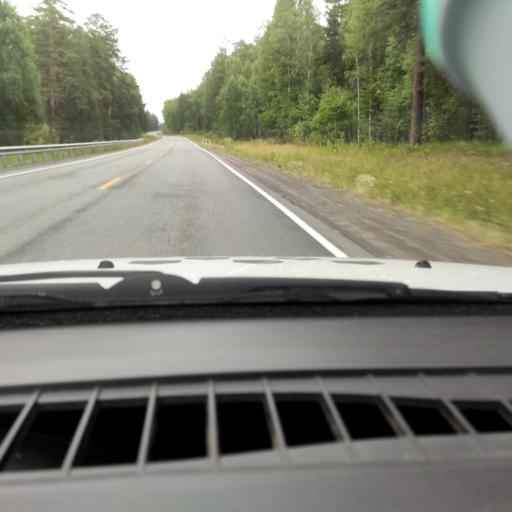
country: RU
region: Chelyabinsk
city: Karabash
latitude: 55.3065
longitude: 60.2053
